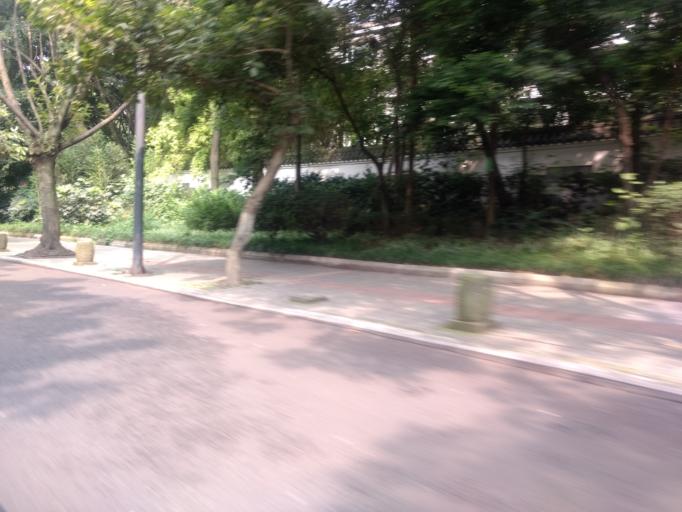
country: CN
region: Sichuan
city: Chengdu
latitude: 30.6613
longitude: 104.0306
